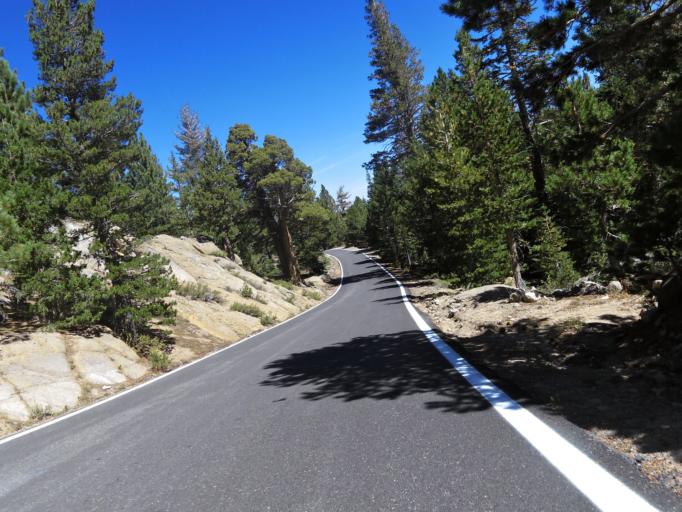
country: US
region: Nevada
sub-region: Douglas County
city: Gardnerville Ranchos
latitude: 38.5696
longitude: -119.8073
